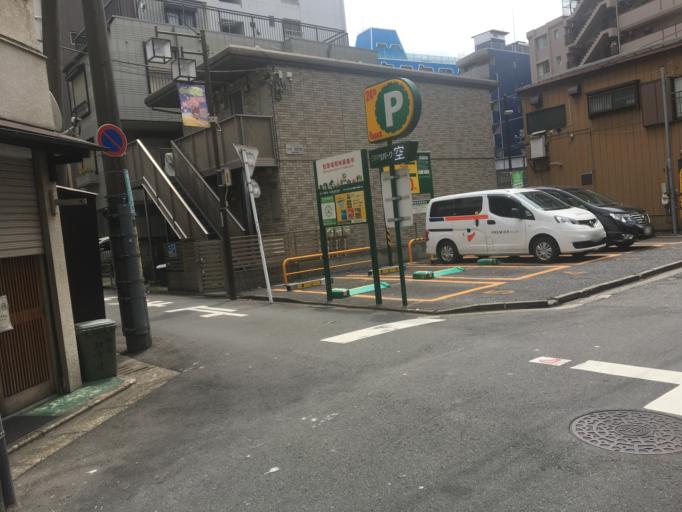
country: JP
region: Saitama
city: Kawaguchi
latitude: 35.8143
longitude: 139.7036
